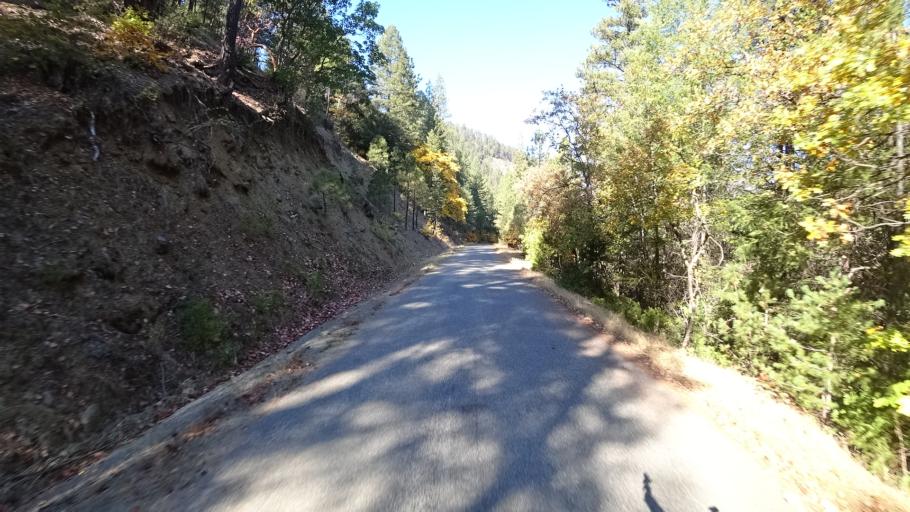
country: US
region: California
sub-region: Siskiyou County
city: Happy Camp
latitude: 41.7652
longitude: -123.0232
